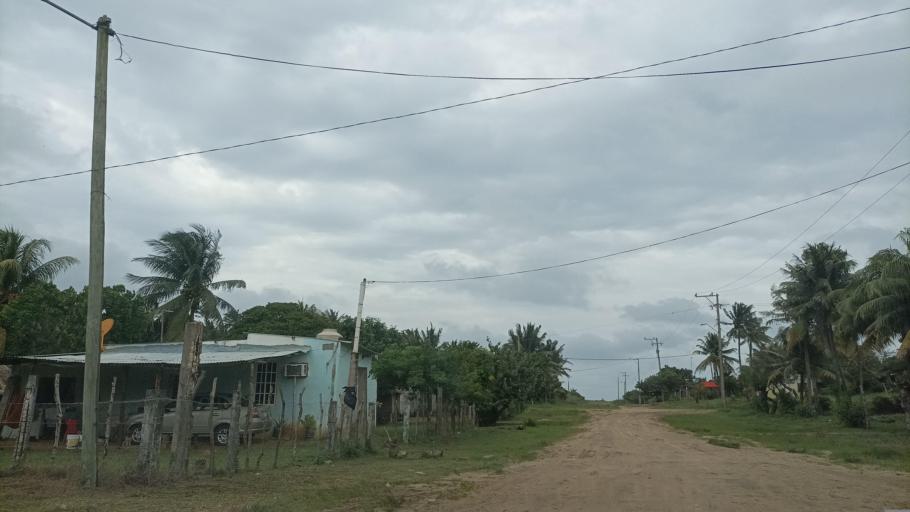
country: MX
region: Veracruz
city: Agua Dulce
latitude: 18.2078
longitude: -94.1406
